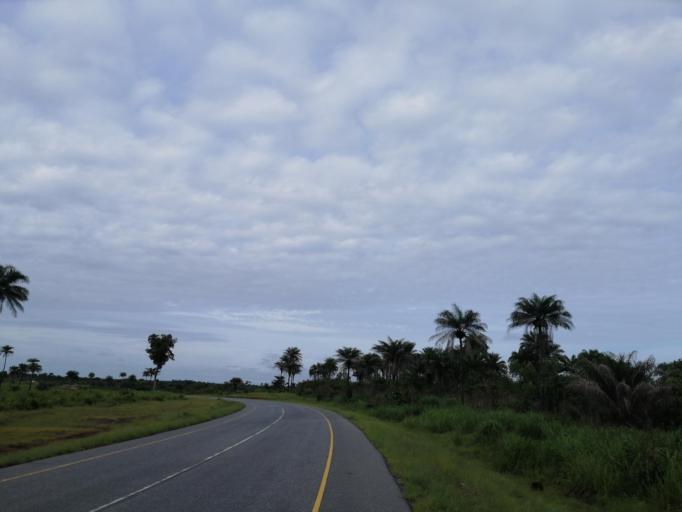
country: SL
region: Northern Province
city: Port Loko
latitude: 8.7918
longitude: -12.8472
